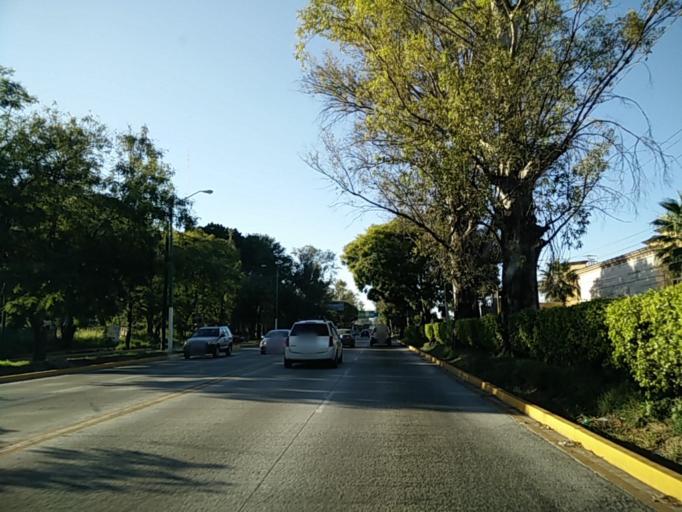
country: MX
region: Jalisco
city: Zapopan2
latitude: 20.6900
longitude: -103.4484
